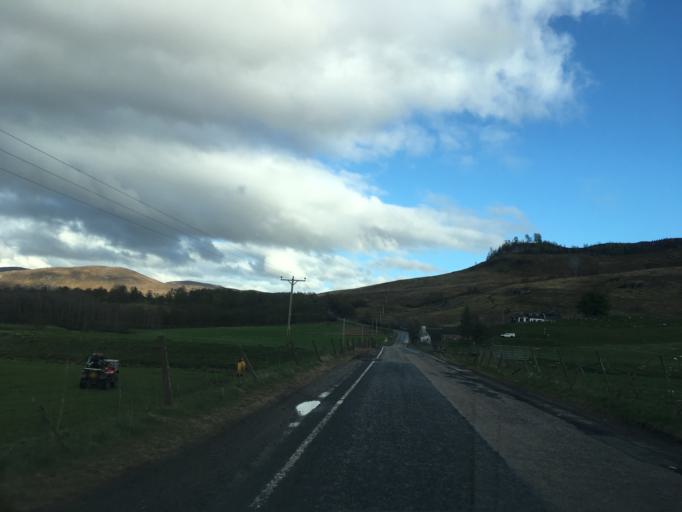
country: GB
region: Scotland
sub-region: Highland
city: Kingussie
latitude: 57.0100
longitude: -4.2669
